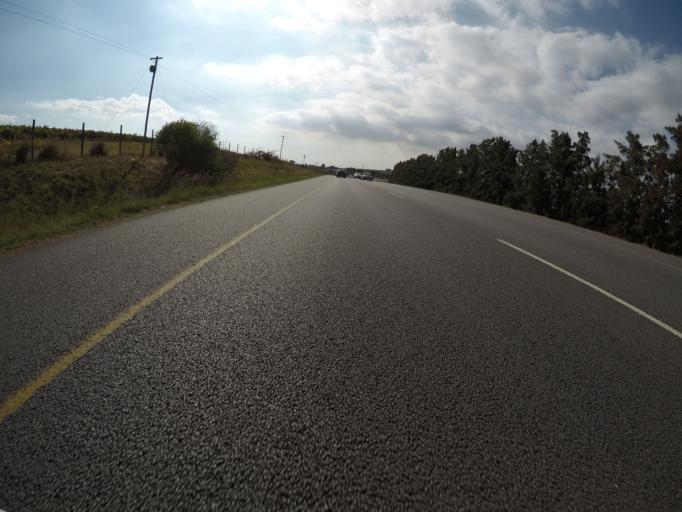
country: ZA
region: Western Cape
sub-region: Cape Winelands District Municipality
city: Stellenbosch
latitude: -33.8806
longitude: 18.8172
